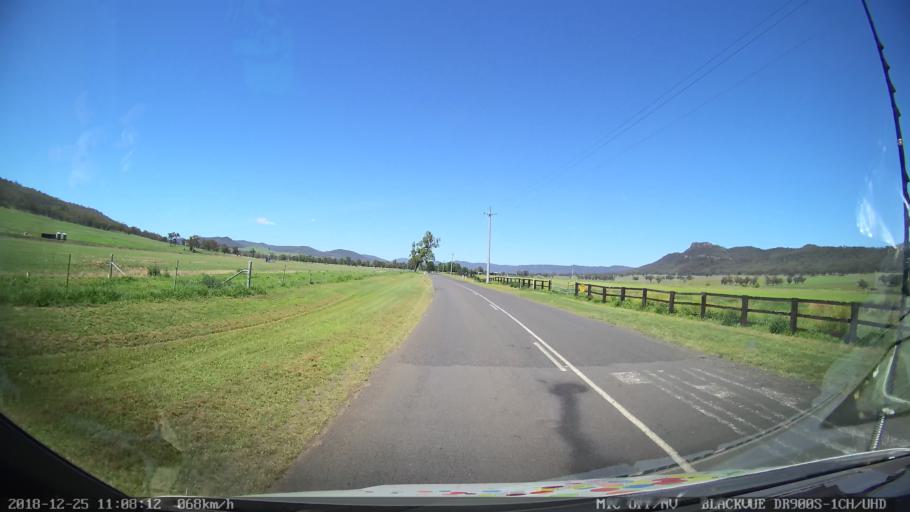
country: AU
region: New South Wales
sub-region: Upper Hunter Shire
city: Merriwa
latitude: -32.4004
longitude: 150.1266
